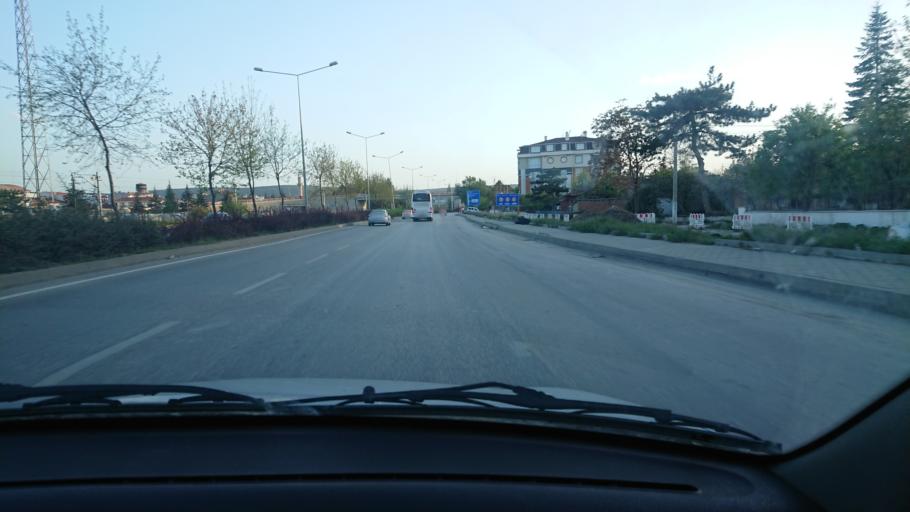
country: TR
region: Eskisehir
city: Eskisehir
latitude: 39.7710
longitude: 30.4826
